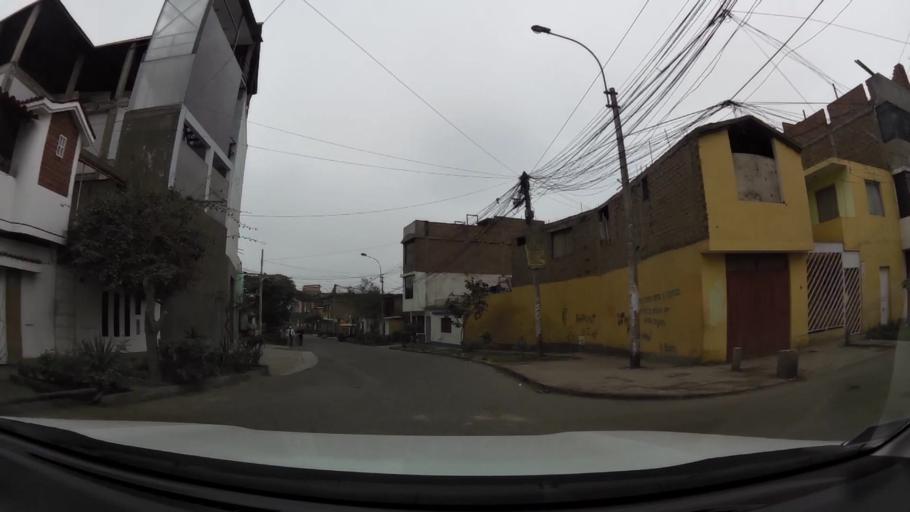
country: PE
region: Lima
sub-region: Lima
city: Surco
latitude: -12.1528
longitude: -76.9655
